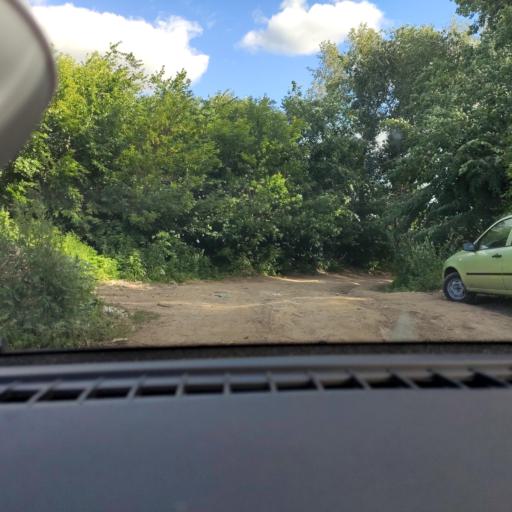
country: RU
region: Samara
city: Samara
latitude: 53.1777
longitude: 50.2375
